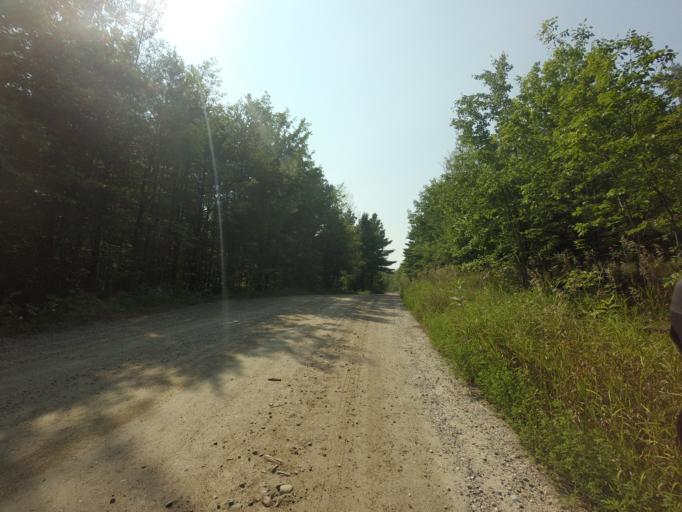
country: CA
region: Ontario
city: Skatepark
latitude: 44.7253
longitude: -76.7841
